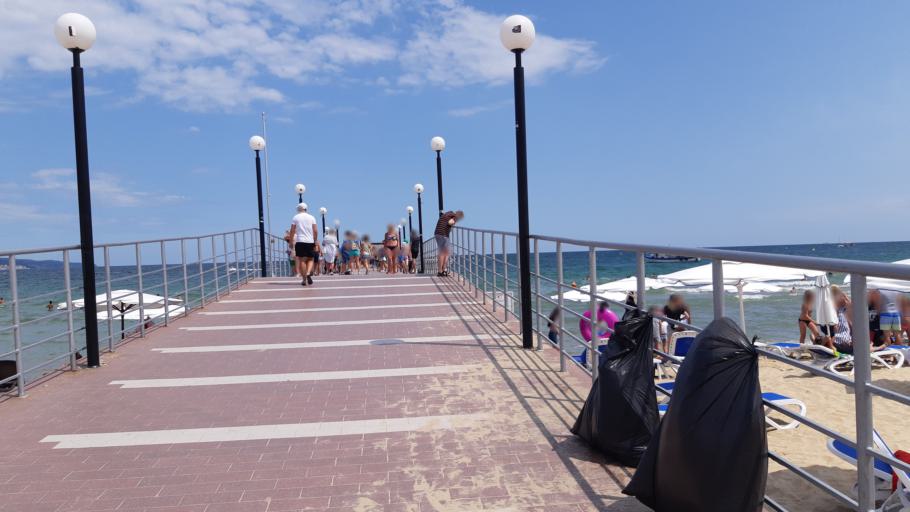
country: BG
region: Burgas
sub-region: Obshtina Nesebur
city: Nesebar
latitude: 42.6939
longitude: 27.7156
